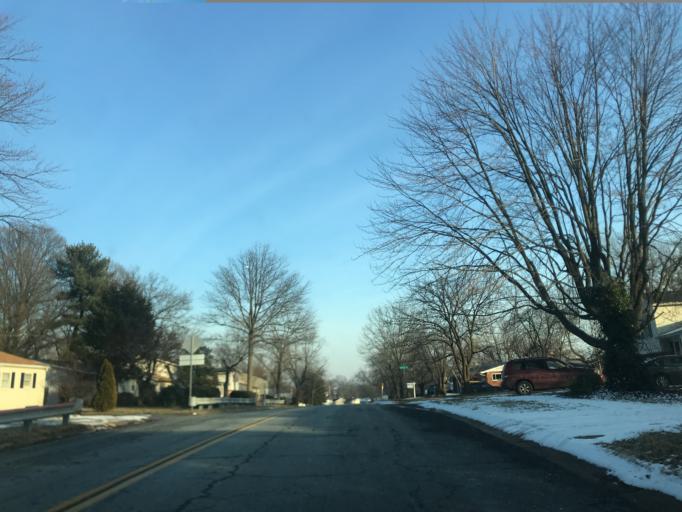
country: US
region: Maryland
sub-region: Harford County
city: Edgewood
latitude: 39.4257
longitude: -76.3067
